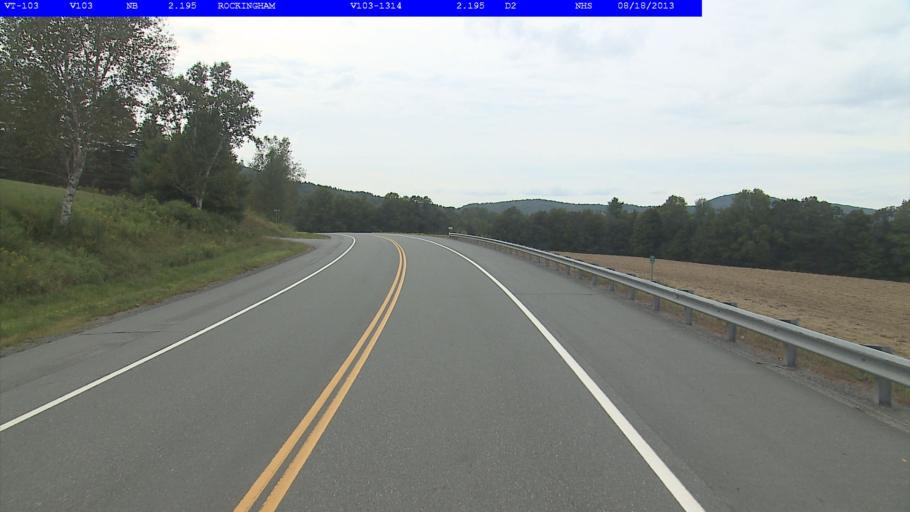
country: US
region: Vermont
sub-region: Windham County
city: Rockingham
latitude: 43.1942
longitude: -72.4958
